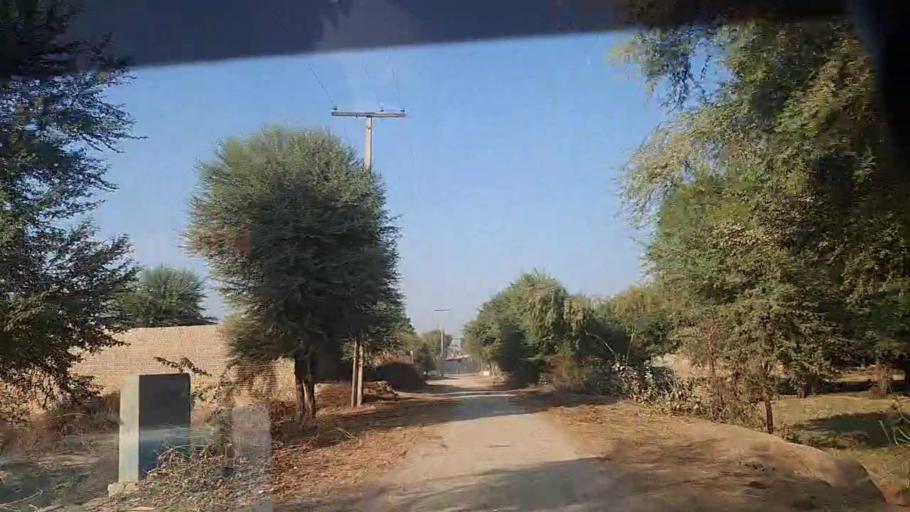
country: PK
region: Sindh
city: Sobhadero
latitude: 27.2541
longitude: 68.3507
